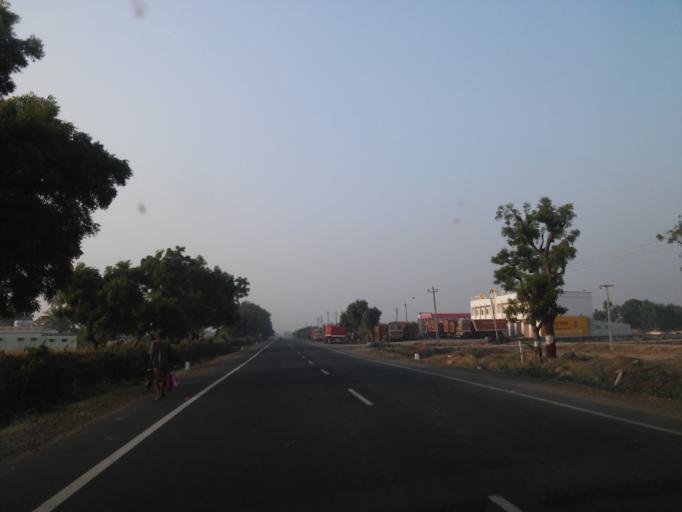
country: IN
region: Gujarat
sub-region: Kachchh
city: Mandvi
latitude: 22.8589
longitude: 69.3849
